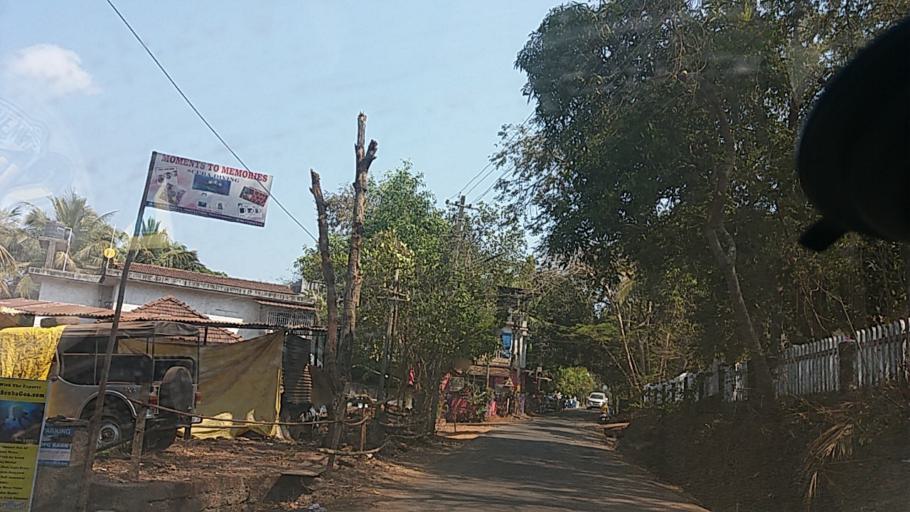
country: IN
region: Goa
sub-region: North Goa
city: Saligao
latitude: 15.5430
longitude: 73.7814
